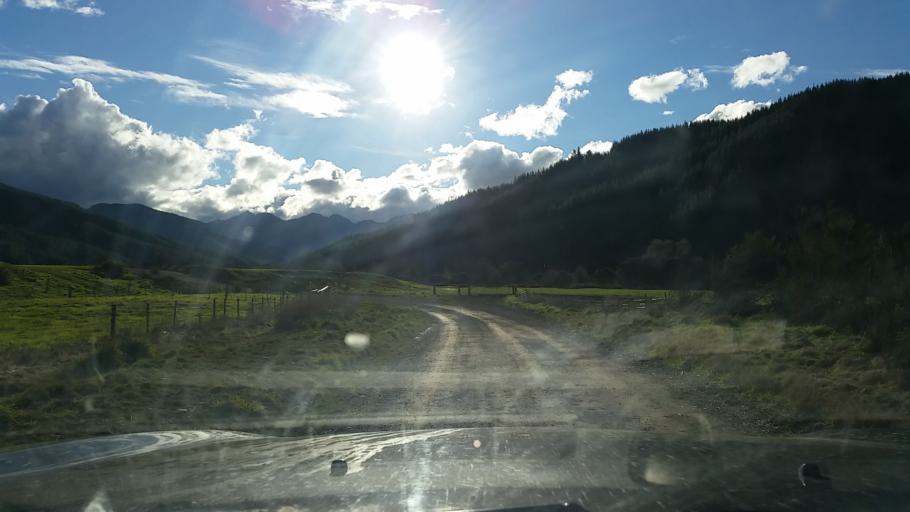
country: NZ
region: Nelson
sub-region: Nelson City
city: Nelson
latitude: -41.5654
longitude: 173.4486
